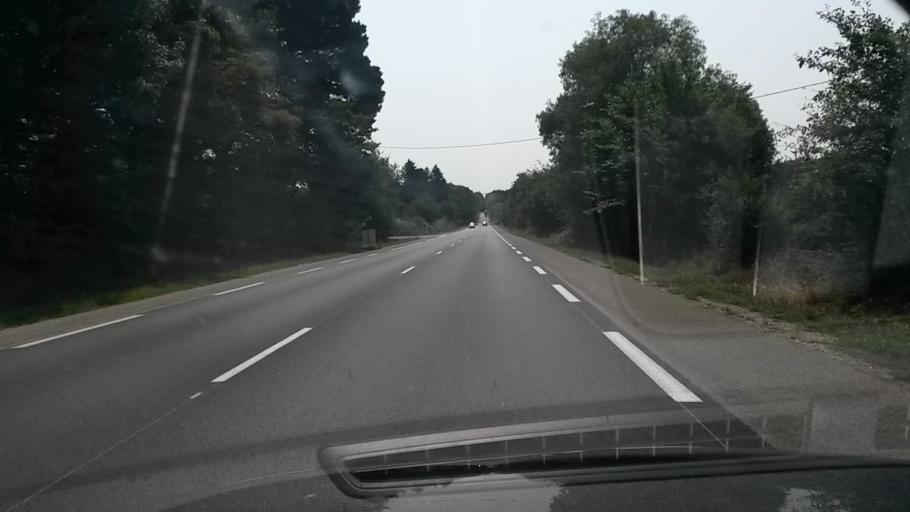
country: FR
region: Pays de la Loire
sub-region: Departement de la Mayenne
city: Chateau-Gontier
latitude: 47.8495
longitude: -0.6951
